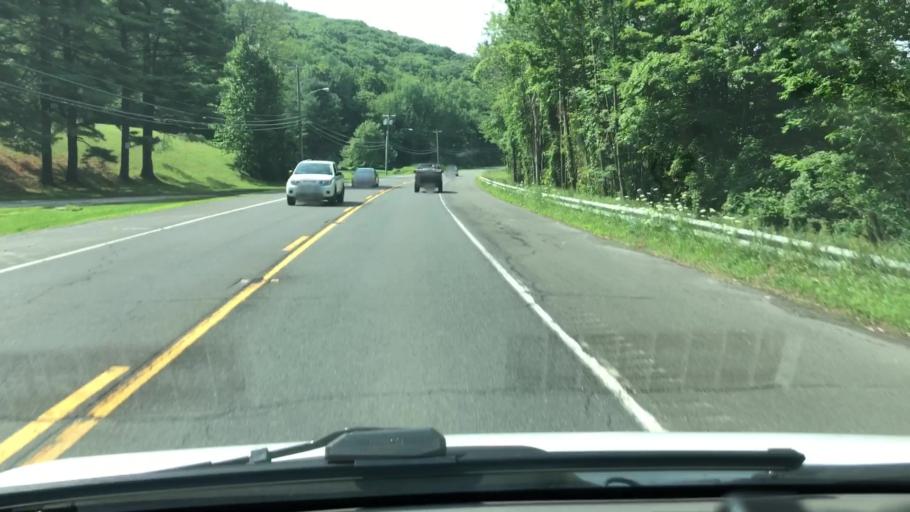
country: US
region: Massachusetts
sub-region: Berkshire County
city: Lanesborough
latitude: 42.5115
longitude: -73.1926
